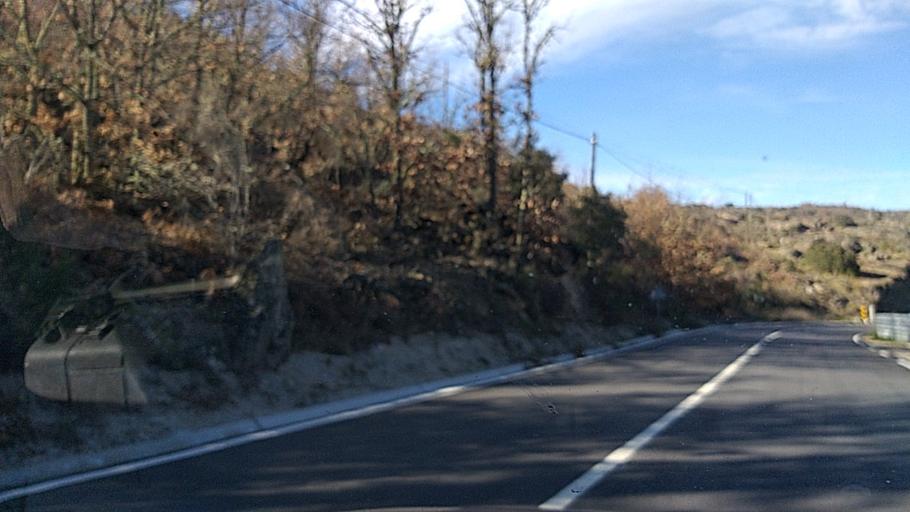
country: ES
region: Castille and Leon
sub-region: Provincia de Salamanca
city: Fuentes de Onoro
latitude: 40.6117
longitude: -6.9208
